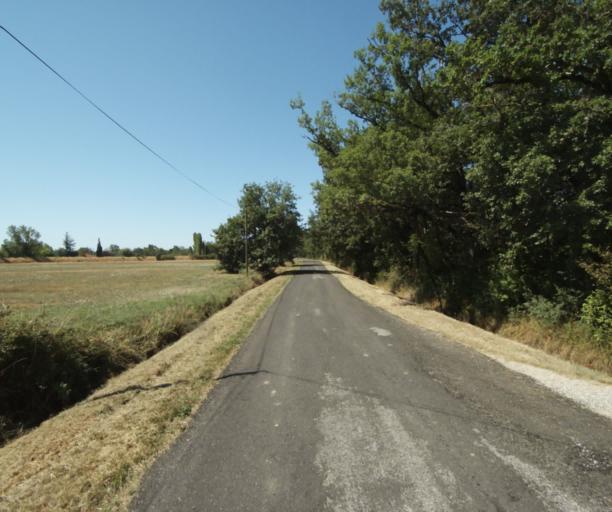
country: FR
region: Midi-Pyrenees
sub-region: Departement de la Haute-Garonne
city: Revel
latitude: 43.4689
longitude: 1.9787
